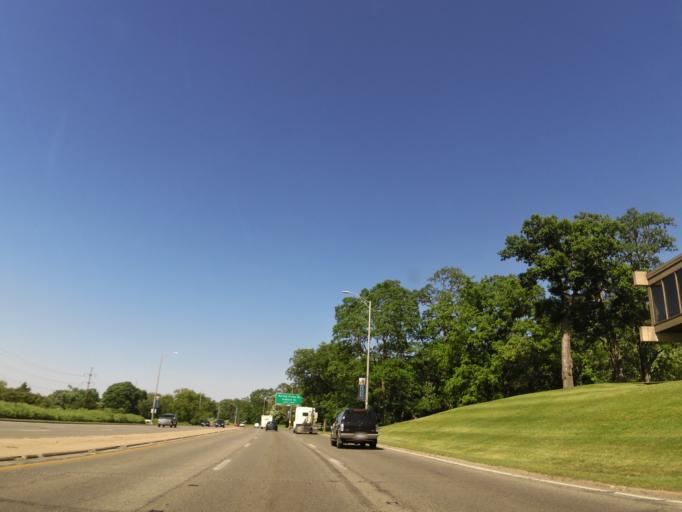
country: US
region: Illinois
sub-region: Winnebago County
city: Rockford
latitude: 42.2827
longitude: -89.0686
